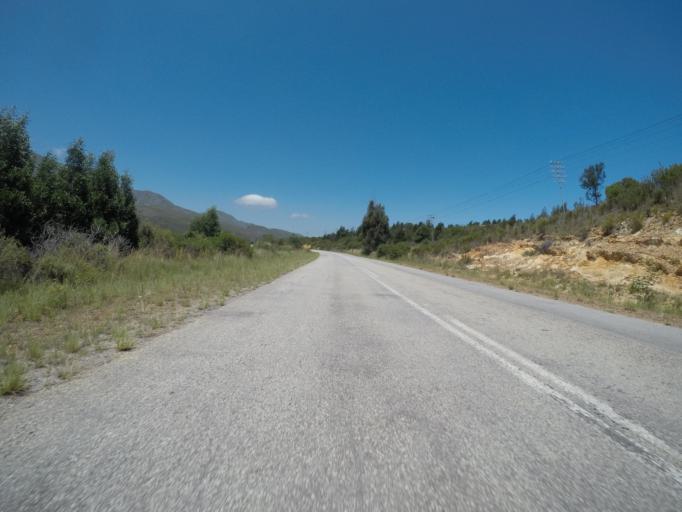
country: ZA
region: Eastern Cape
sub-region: Cacadu District Municipality
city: Kareedouw
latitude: -33.9137
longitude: 24.1804
